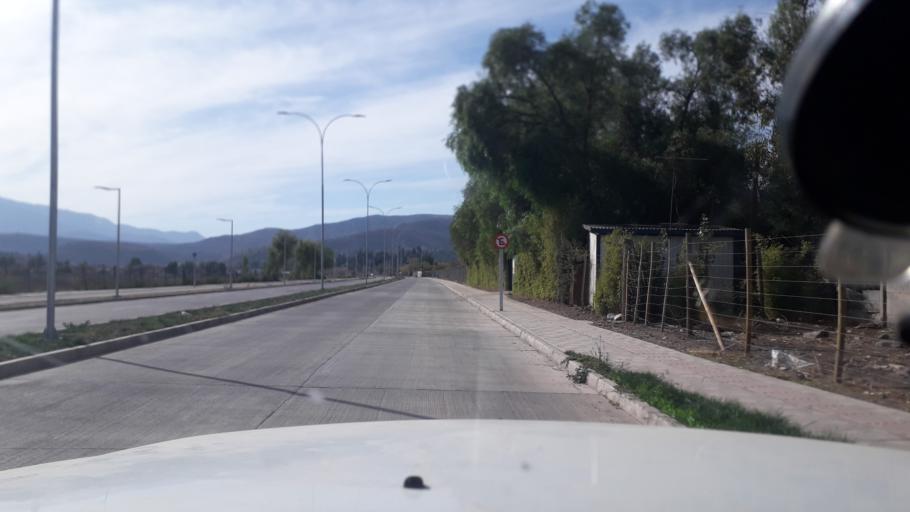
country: CL
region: Valparaiso
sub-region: Provincia de San Felipe
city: San Felipe
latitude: -32.7482
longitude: -70.7107
